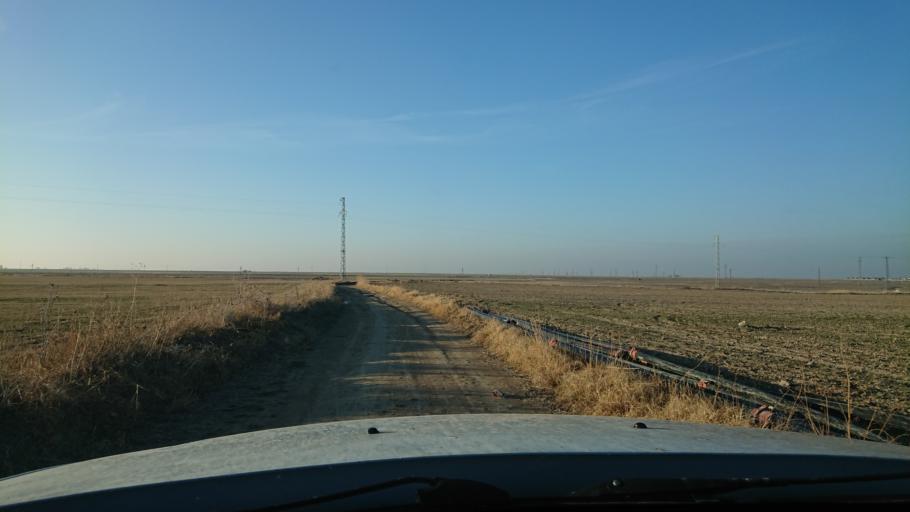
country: TR
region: Aksaray
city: Sultanhani
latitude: 38.2696
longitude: 33.5176
